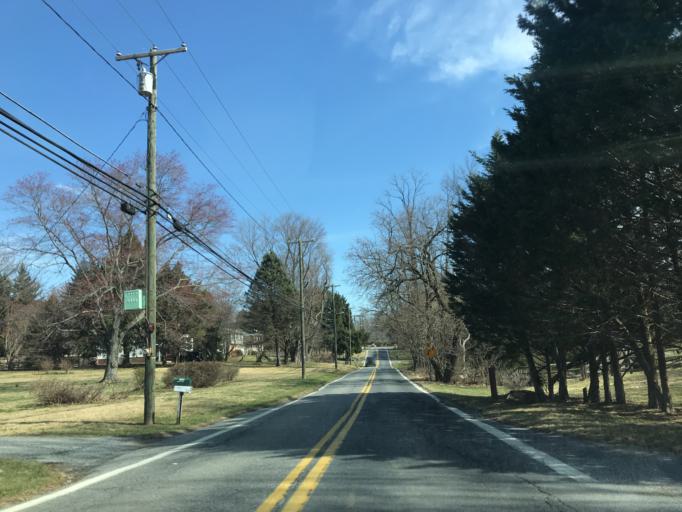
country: US
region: Maryland
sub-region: Montgomery County
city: Ashton-Sandy Spring
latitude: 39.1372
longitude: -76.9920
